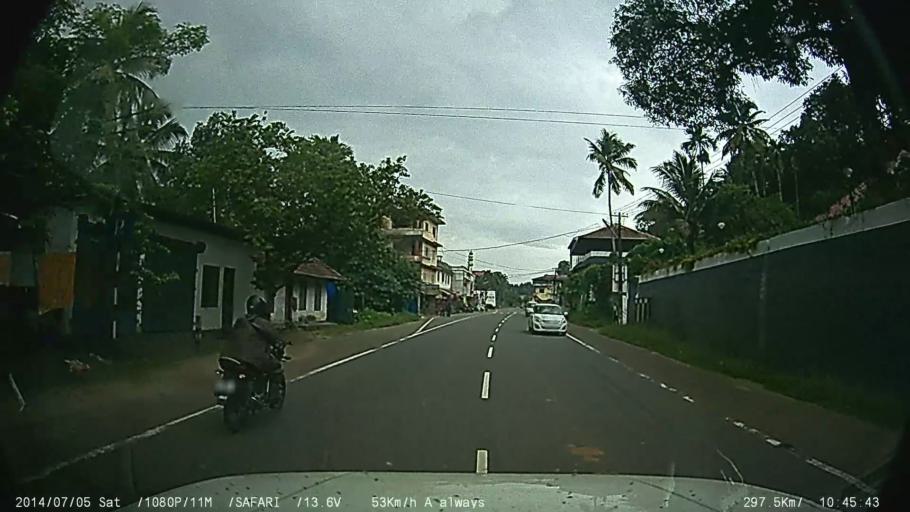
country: IN
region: Kerala
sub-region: Ernakulam
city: Muvattupula
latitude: 9.9766
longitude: 76.5919
